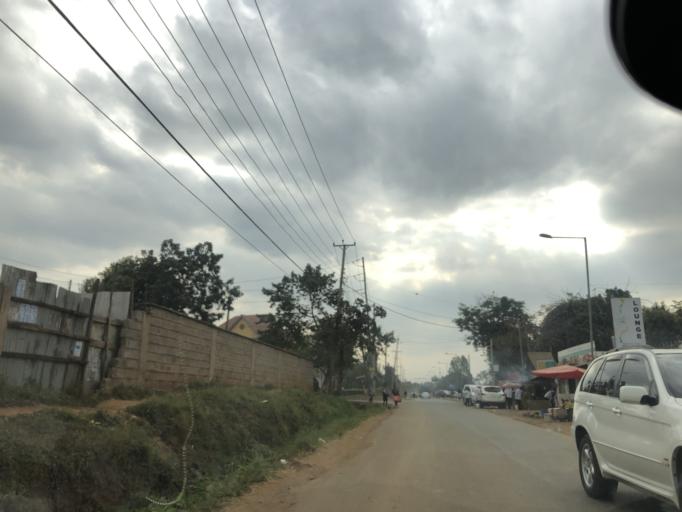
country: KE
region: Kiambu
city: Kiambu
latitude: -1.2101
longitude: 36.8846
